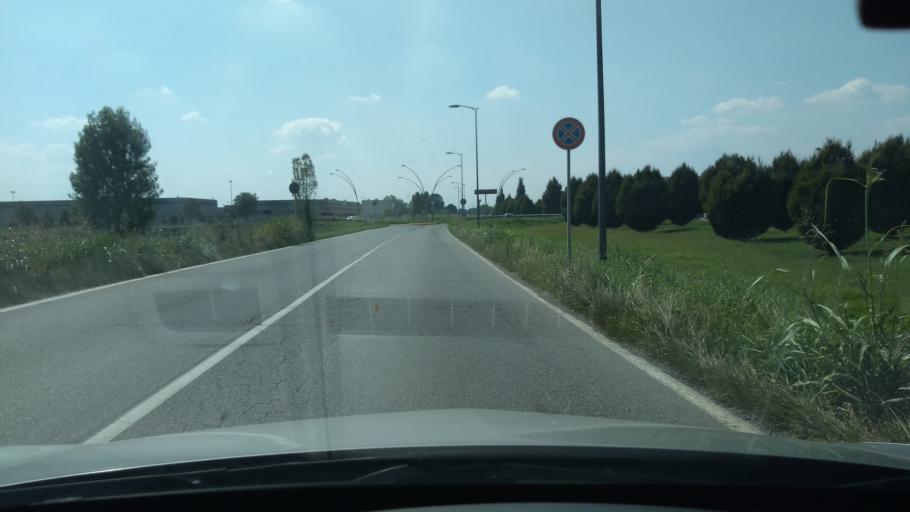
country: IT
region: Lombardy
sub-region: Provincia di Bergamo
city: Ghisalba
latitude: 45.5914
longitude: 9.7668
